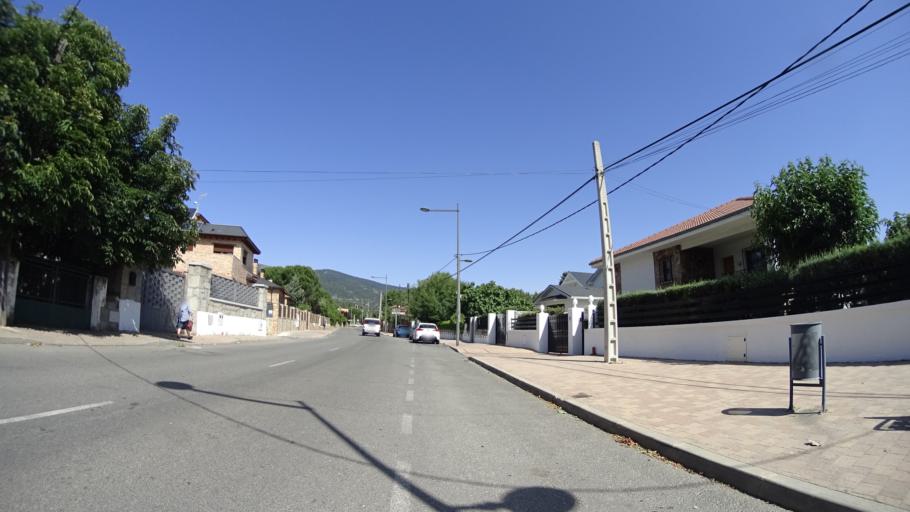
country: ES
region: Madrid
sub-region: Provincia de Madrid
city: Guadarrama
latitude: 40.6776
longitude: -4.0924
